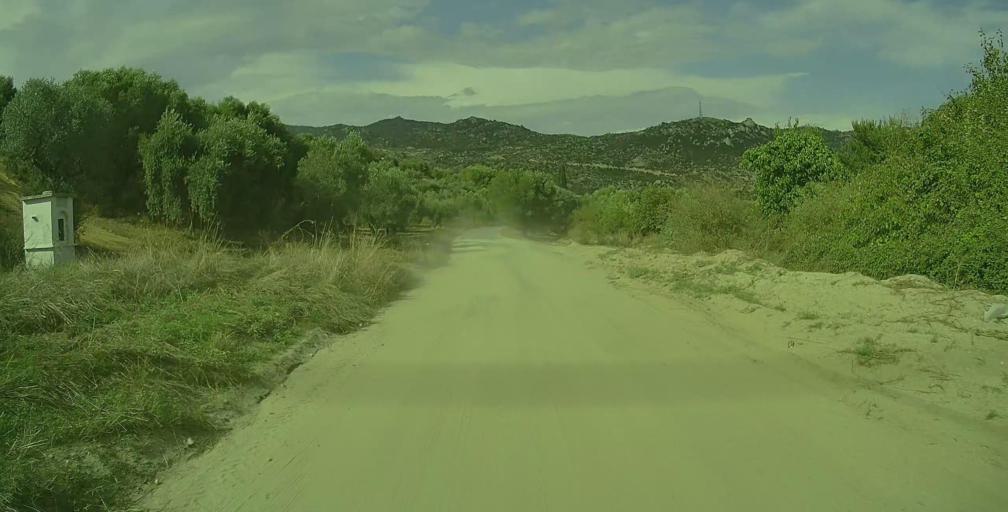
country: GR
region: Central Macedonia
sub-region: Nomos Chalkidikis
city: Sykia
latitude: 40.0341
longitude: 23.9437
